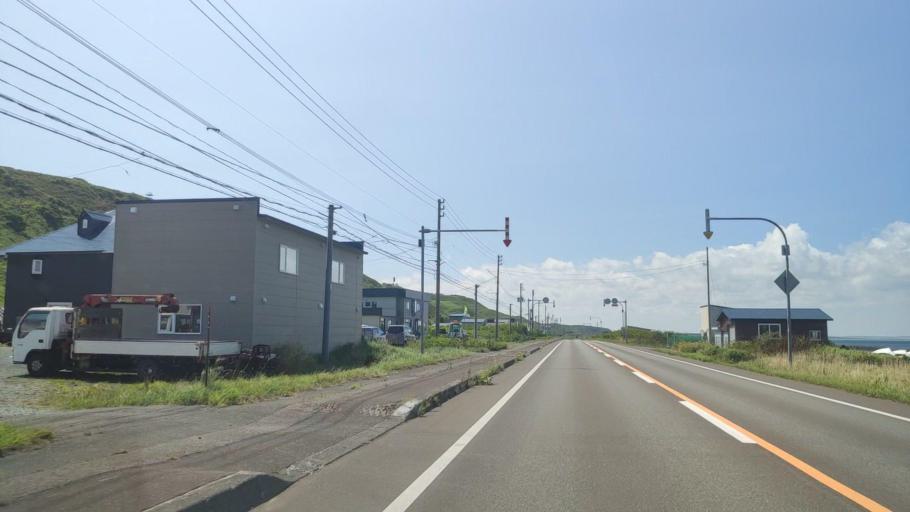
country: JP
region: Hokkaido
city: Makubetsu
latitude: 45.4473
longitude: 141.8696
